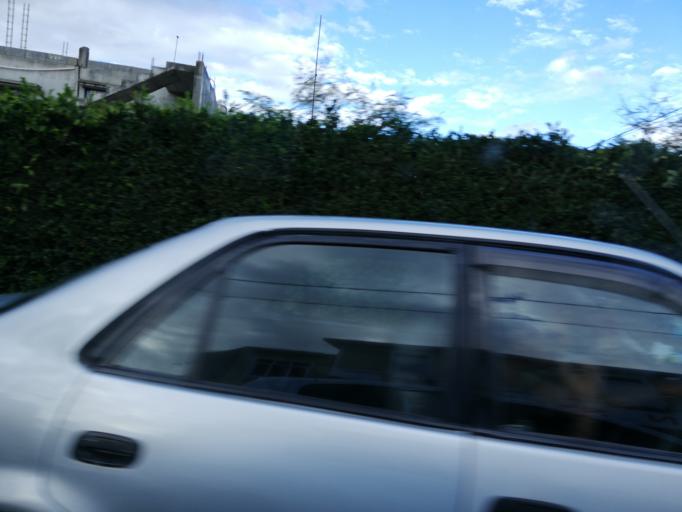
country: MU
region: Plaines Wilhems
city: Ebene
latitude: -20.2349
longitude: 57.4595
